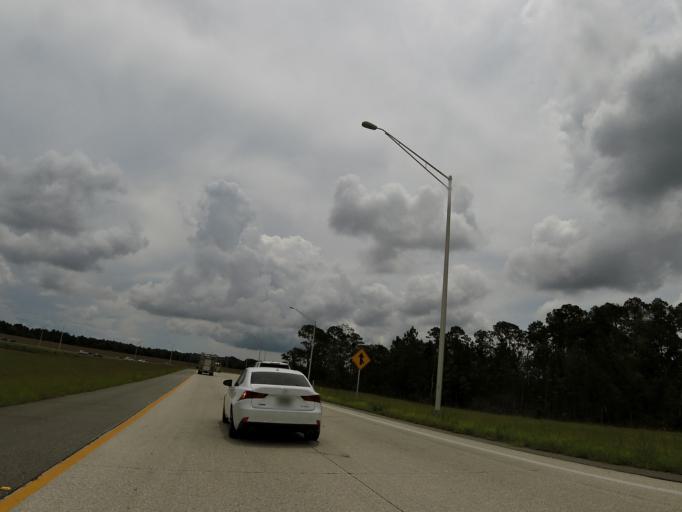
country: US
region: Florida
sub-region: Saint Johns County
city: Fruit Cove
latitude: 30.1098
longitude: -81.5128
